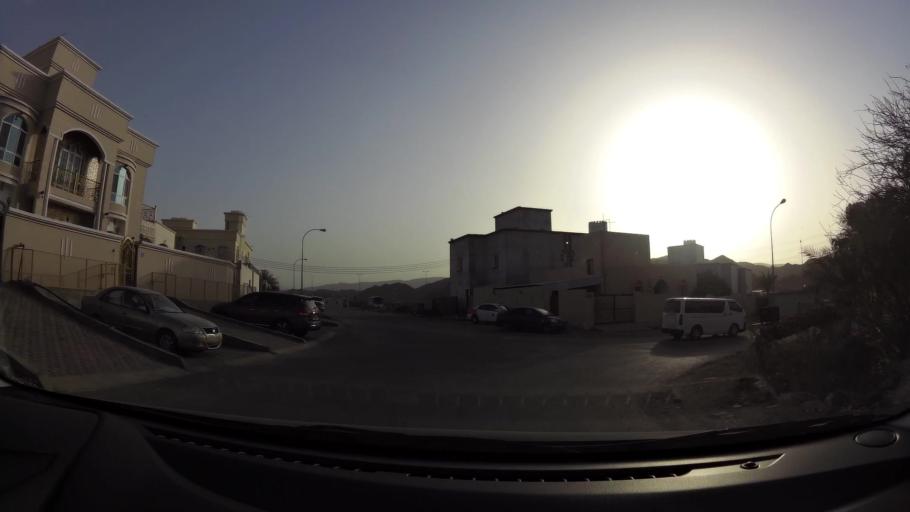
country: OM
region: Muhafazat Masqat
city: Bawshar
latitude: 23.5134
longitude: 58.3447
